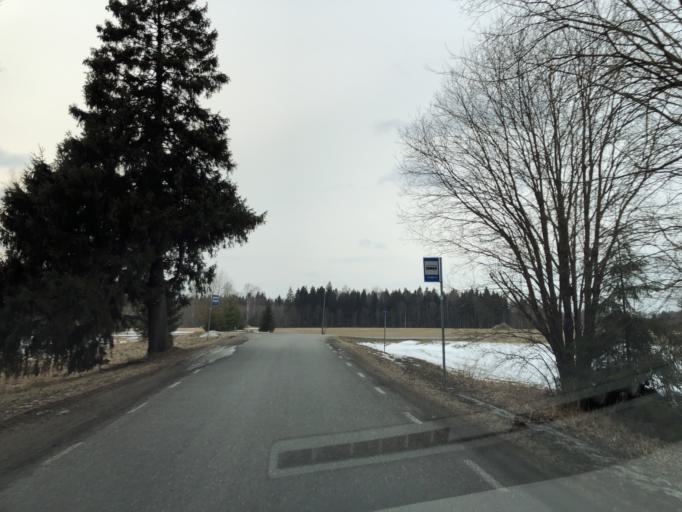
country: EE
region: Paernumaa
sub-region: Vaendra vald (alev)
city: Vandra
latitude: 58.6670
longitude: 25.0172
